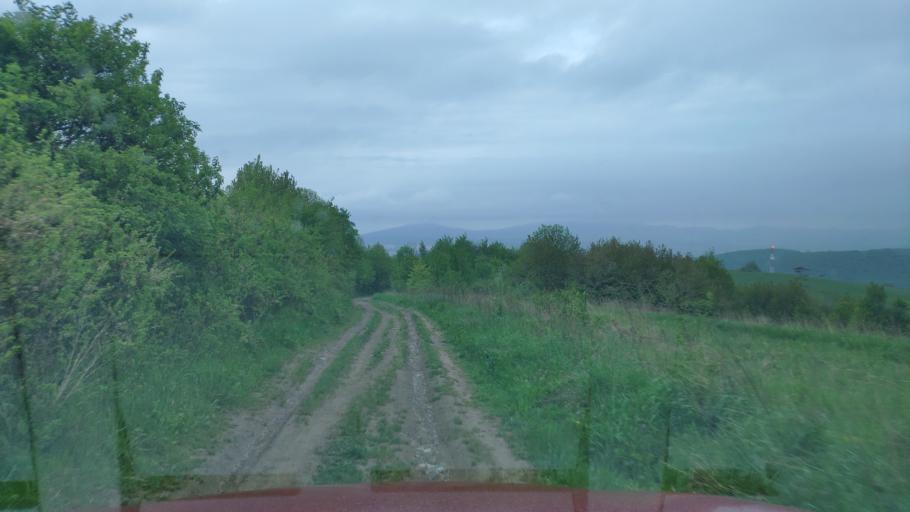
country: SK
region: Kosicky
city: Kosice
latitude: 48.7680
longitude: 21.2071
